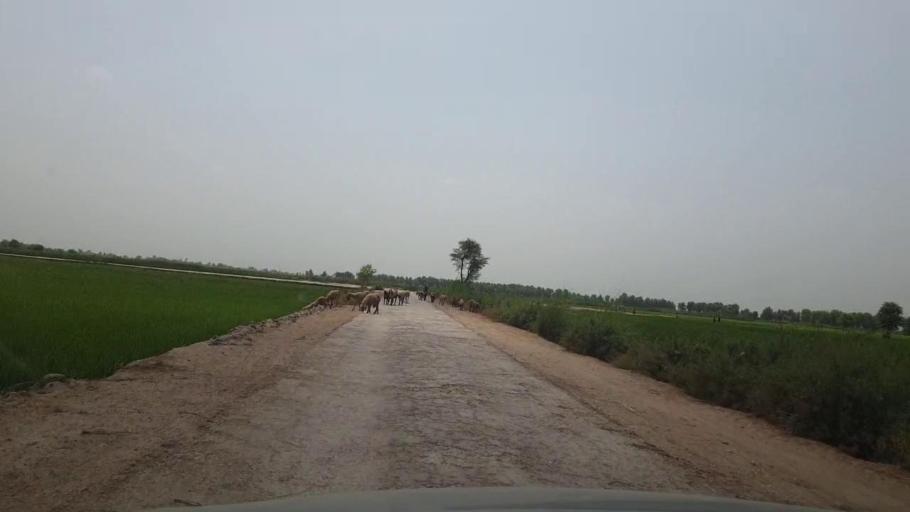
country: PK
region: Sindh
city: Garhi Yasin
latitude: 27.9415
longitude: 68.3801
